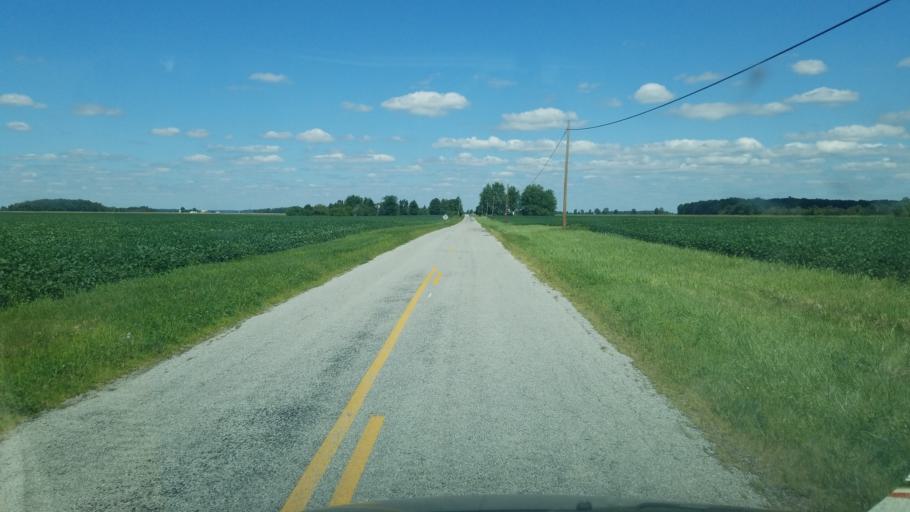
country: US
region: Ohio
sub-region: Fulton County
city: Delta
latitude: 41.7088
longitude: -84.0177
